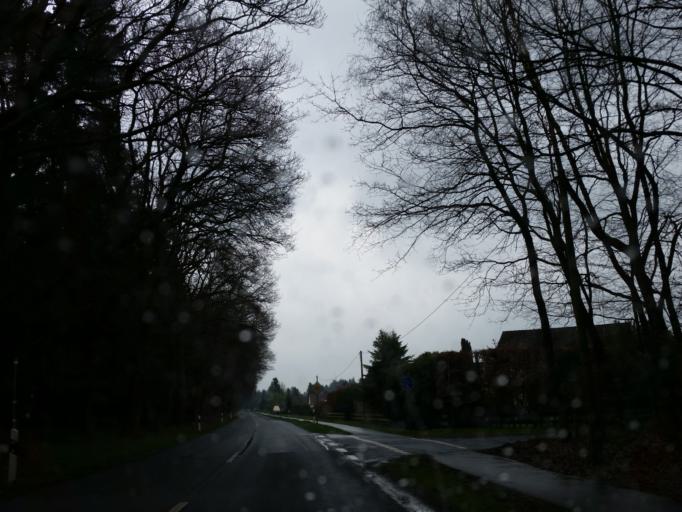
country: DE
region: Lower Saxony
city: Oerel
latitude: 53.4954
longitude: 9.0223
